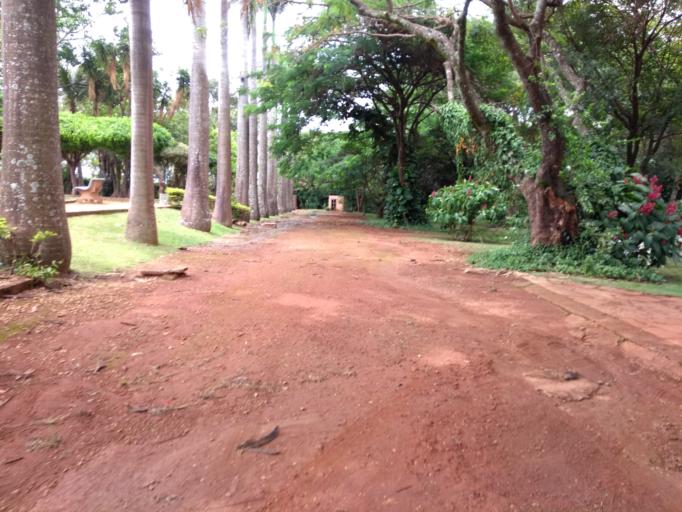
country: BR
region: Federal District
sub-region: Brasilia
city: Brasilia
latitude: -15.9803
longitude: -48.0816
